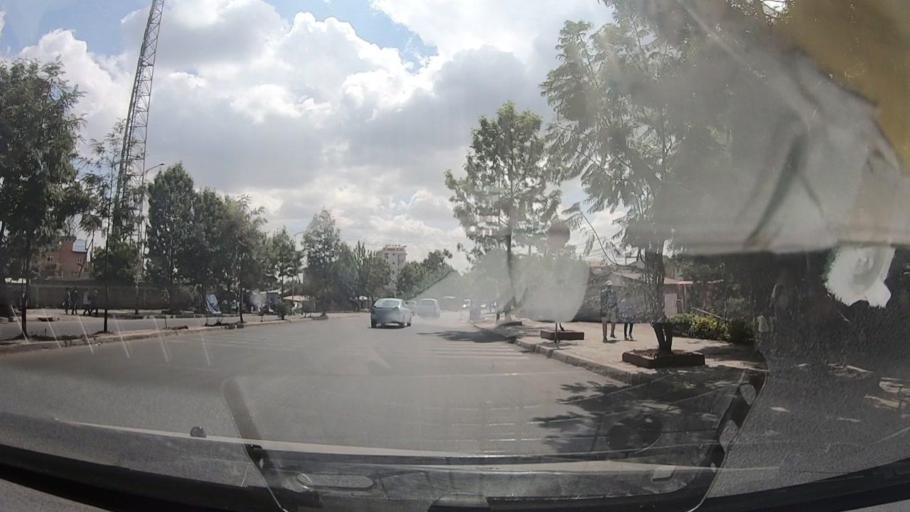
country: ET
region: Adis Abeba
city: Addis Ababa
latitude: 8.9745
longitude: 38.7243
